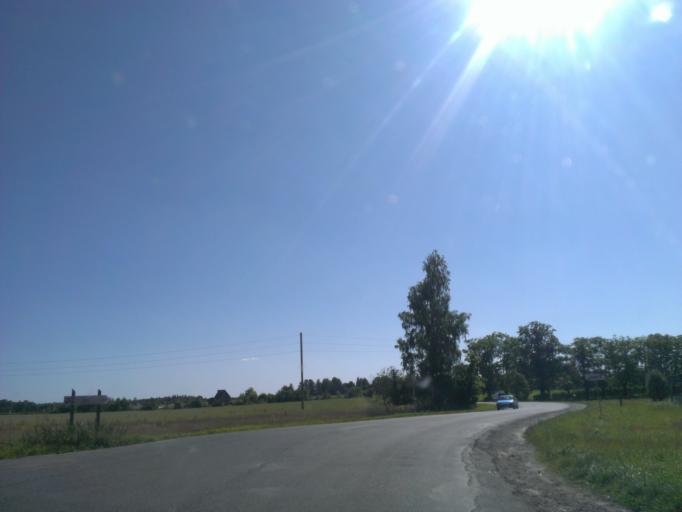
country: LV
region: Sigulda
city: Sigulda
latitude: 57.1410
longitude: 24.8441
